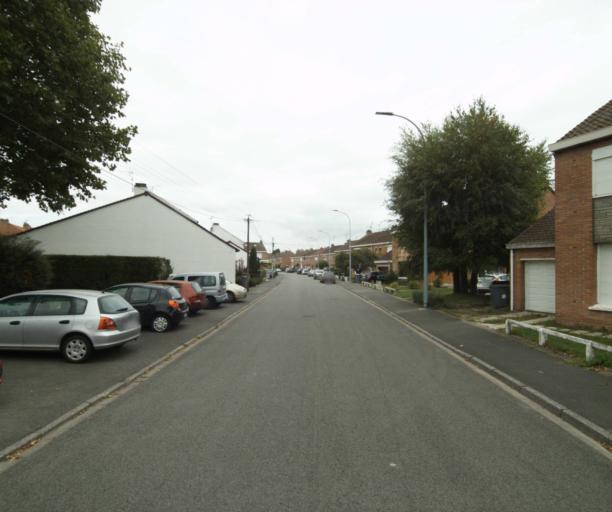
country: FR
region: Nord-Pas-de-Calais
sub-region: Departement du Nord
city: Lambersart
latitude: 50.6574
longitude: 3.0237
